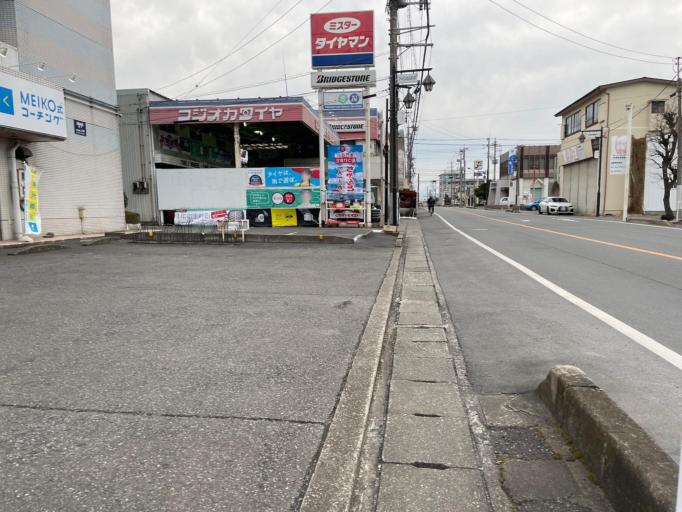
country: JP
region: Gunma
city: Fujioka
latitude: 36.2502
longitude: 139.0812
